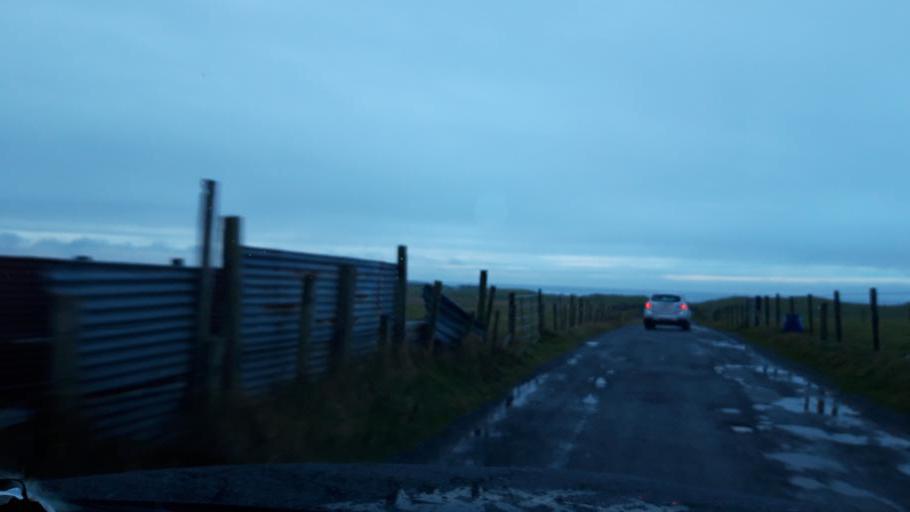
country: IE
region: Ulster
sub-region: County Donegal
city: Ramelton
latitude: 55.2592
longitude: -7.6817
